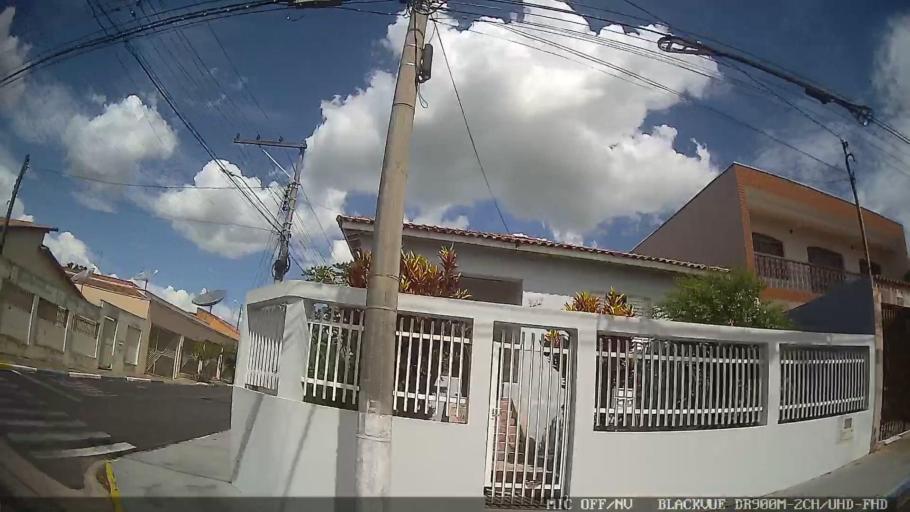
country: BR
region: Sao Paulo
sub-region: Conchas
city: Conchas
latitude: -23.0167
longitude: -48.0094
